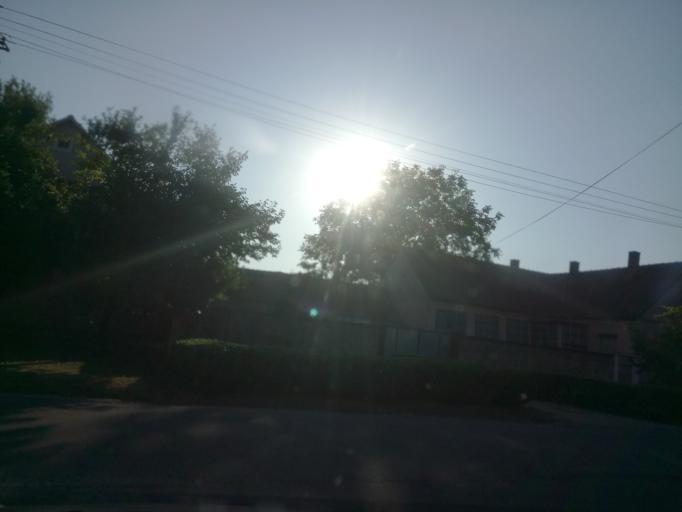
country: RS
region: Autonomna Pokrajina Vojvodina
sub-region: Sremski Okrug
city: Stara Pazova
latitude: 44.9899
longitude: 20.1697
